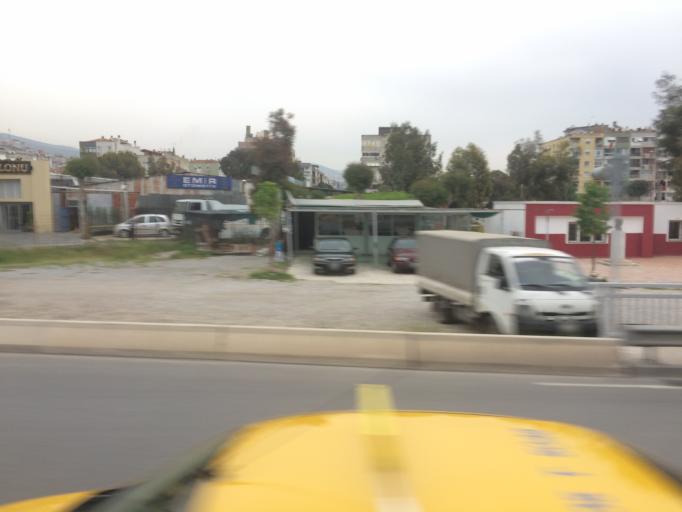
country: TR
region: Izmir
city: Karsiyaka
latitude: 38.4614
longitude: 27.1645
